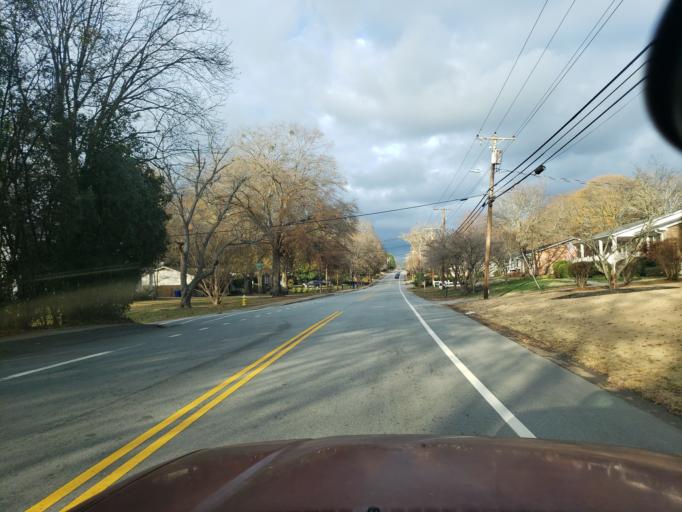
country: US
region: South Carolina
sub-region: Greenville County
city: Greenville
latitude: 34.8290
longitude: -82.3626
